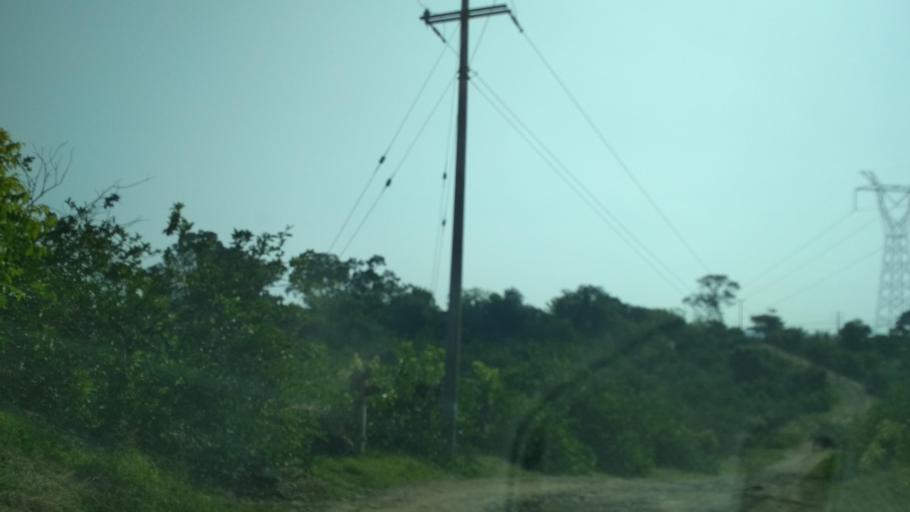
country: MX
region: Puebla
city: San Jose Acateno
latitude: 20.1714
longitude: -97.1743
